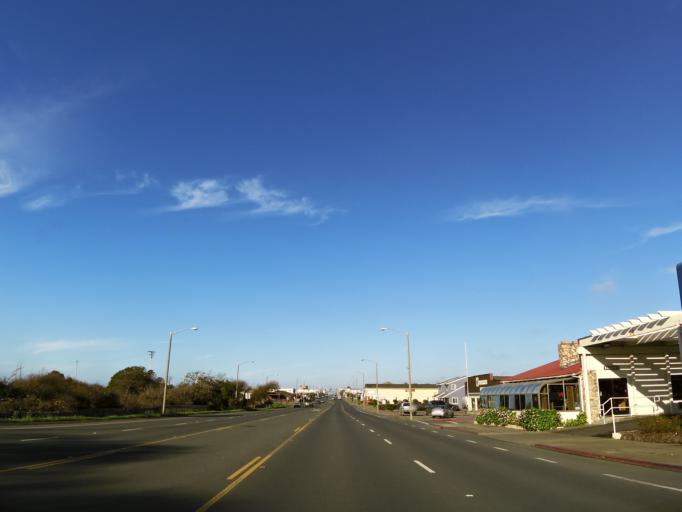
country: US
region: California
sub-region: Mendocino County
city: Fort Bragg
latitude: 39.4375
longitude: -123.8060
